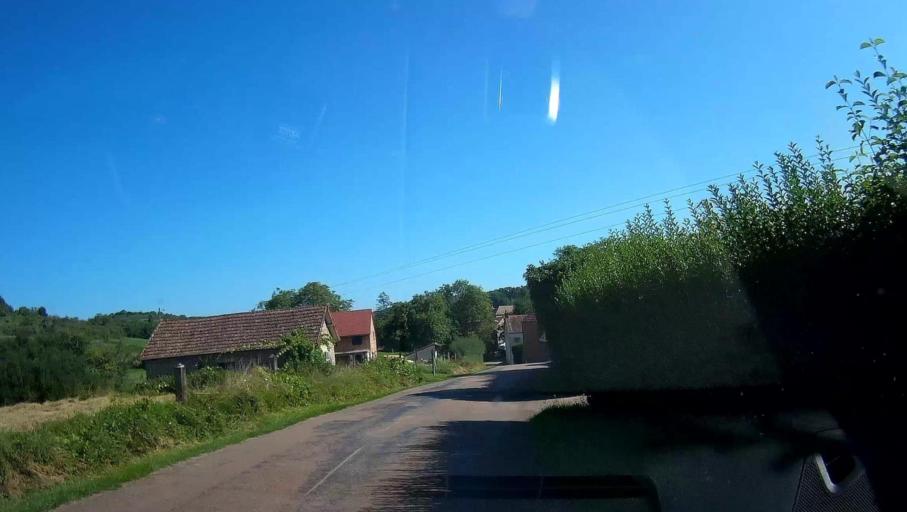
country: FR
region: Bourgogne
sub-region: Departement de Saone-et-Loire
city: Couches
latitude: 46.9055
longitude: 4.5938
